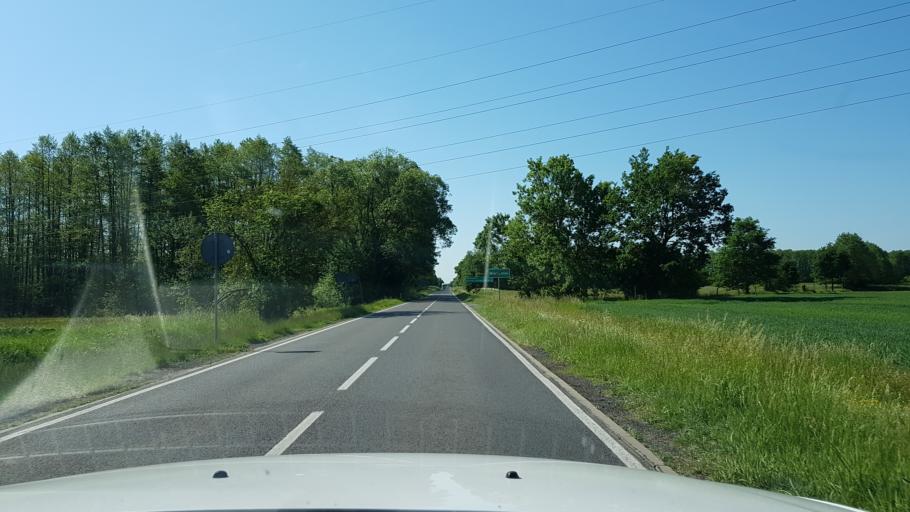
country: PL
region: West Pomeranian Voivodeship
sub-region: Powiat gryfinski
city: Mieszkowice
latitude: 52.8241
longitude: 14.4959
